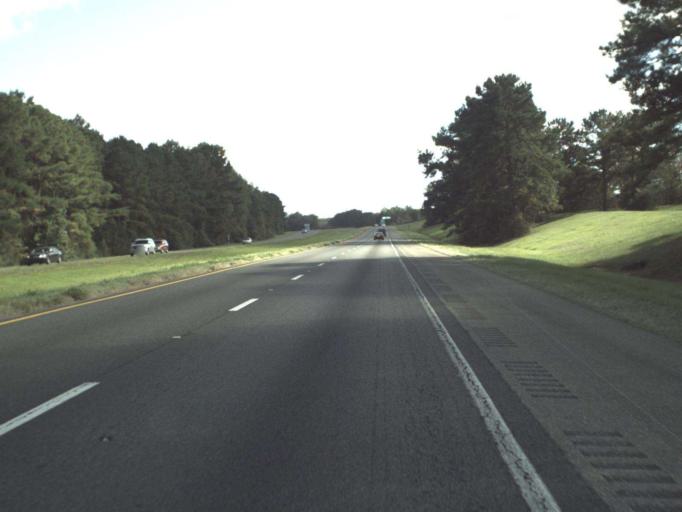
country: US
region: Florida
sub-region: Gadsden County
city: Gretna
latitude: 30.5946
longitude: -84.7234
